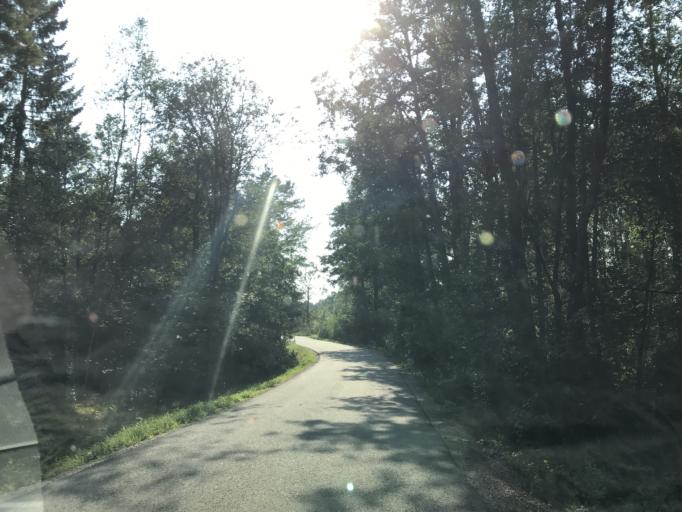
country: SE
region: Stockholm
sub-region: Norrtalje Kommun
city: Bjorko
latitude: 59.8583
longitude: 19.0252
